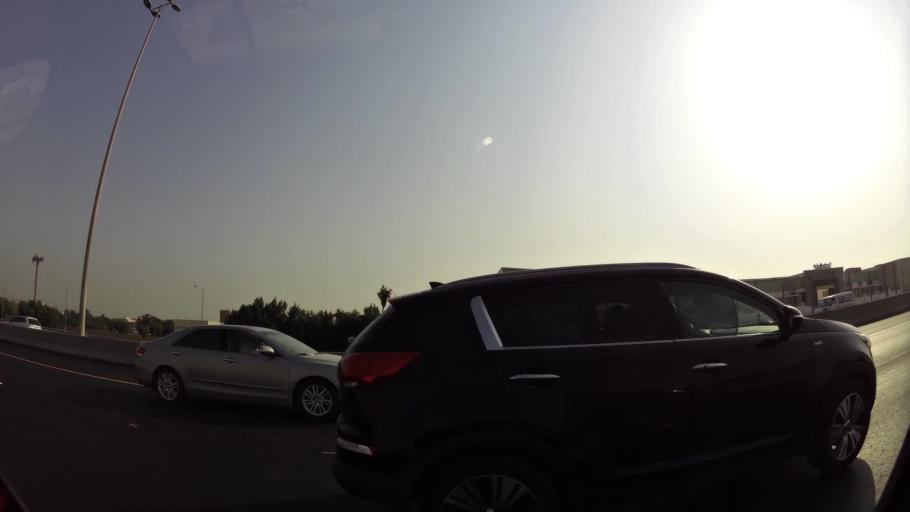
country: KW
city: Al Funaytis
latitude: 29.2163
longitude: 48.1020
